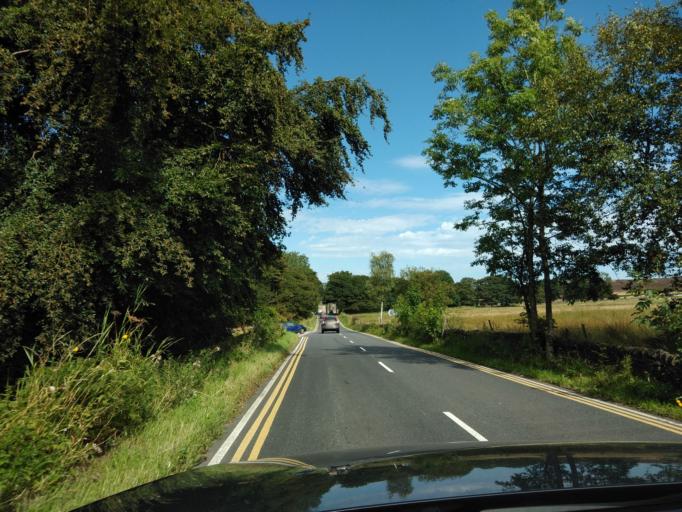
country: GB
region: England
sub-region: Derbyshire
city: Hathersage
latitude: 53.3164
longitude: -1.6001
